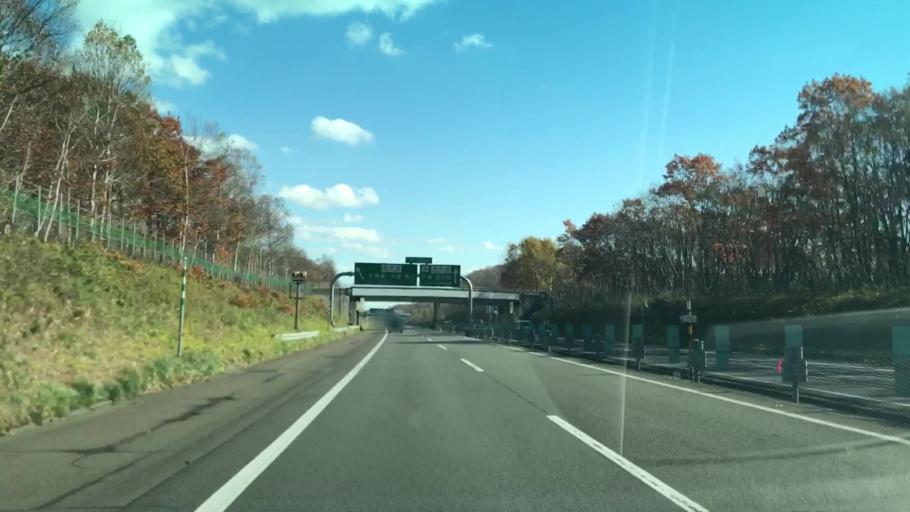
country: JP
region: Hokkaido
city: Chitose
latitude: 42.8485
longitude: 141.5758
